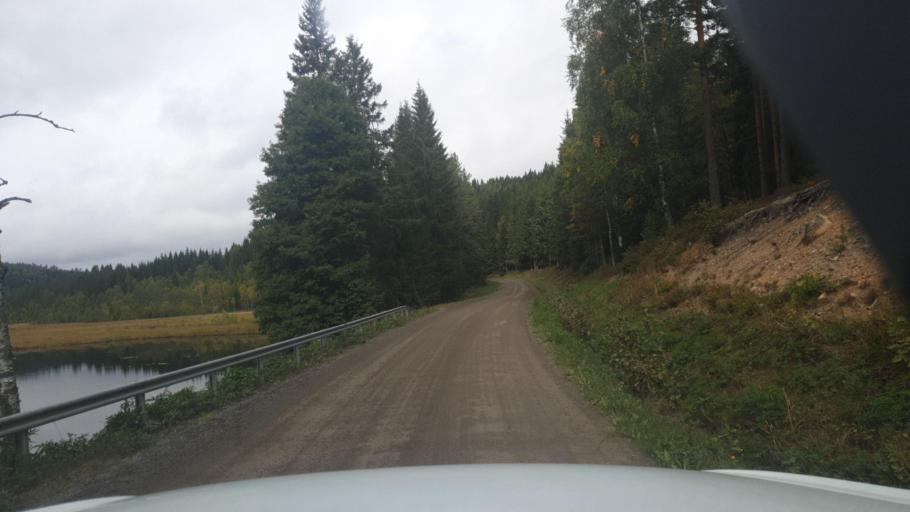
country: SE
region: Vaermland
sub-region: Sunne Kommun
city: Sunne
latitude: 59.8526
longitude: 12.9082
